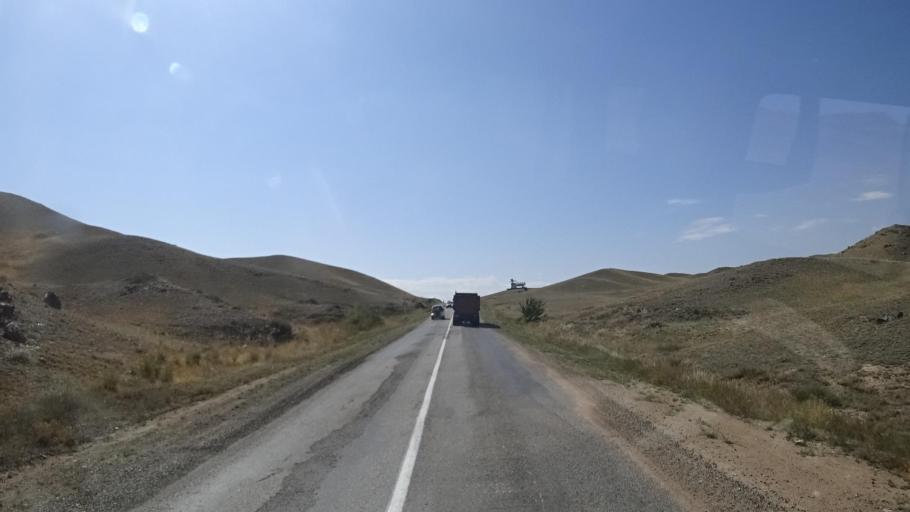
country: KZ
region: Almaty Oblysy
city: Kegen
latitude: 43.3228
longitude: 78.9343
